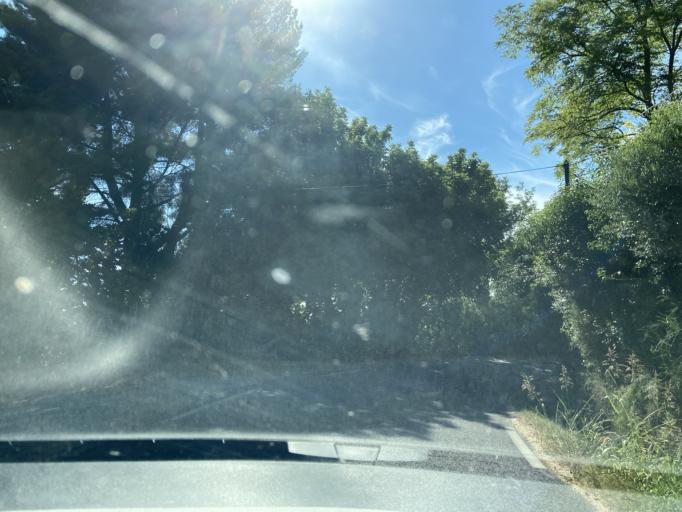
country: FR
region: Provence-Alpes-Cote d'Azur
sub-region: Departement des Bouches-du-Rhone
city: Saint-Chamas
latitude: 43.5604
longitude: 5.0255
